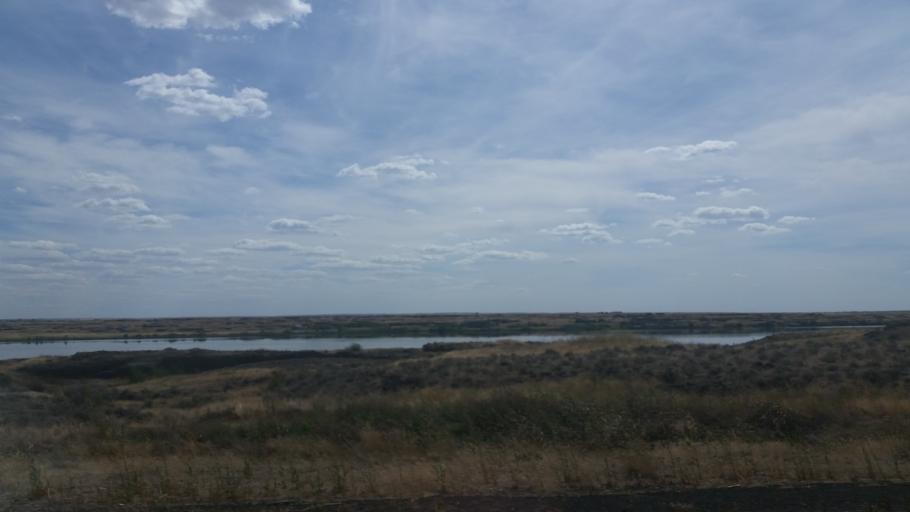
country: US
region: Washington
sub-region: Adams County
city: Ritzville
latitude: 47.2691
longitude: -118.0629
